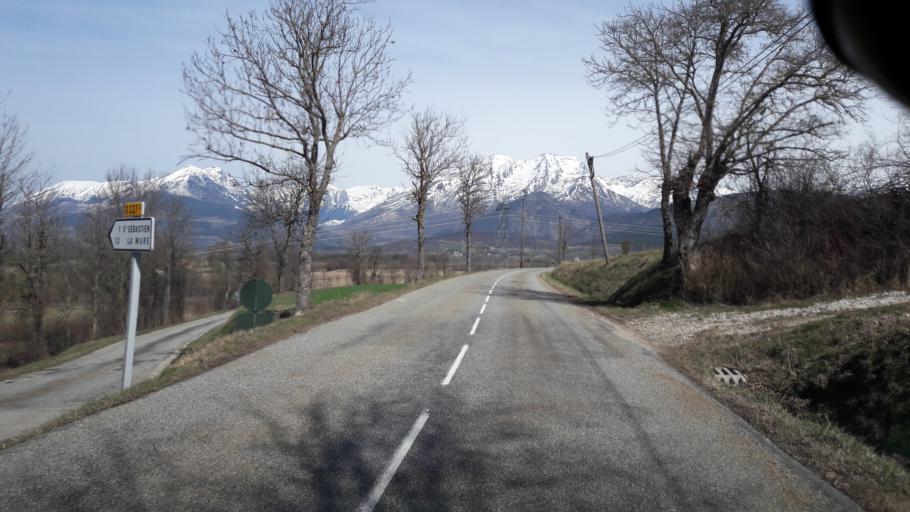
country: FR
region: Rhone-Alpes
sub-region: Departement de l'Isere
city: Mens
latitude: 44.8419
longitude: 5.8023
